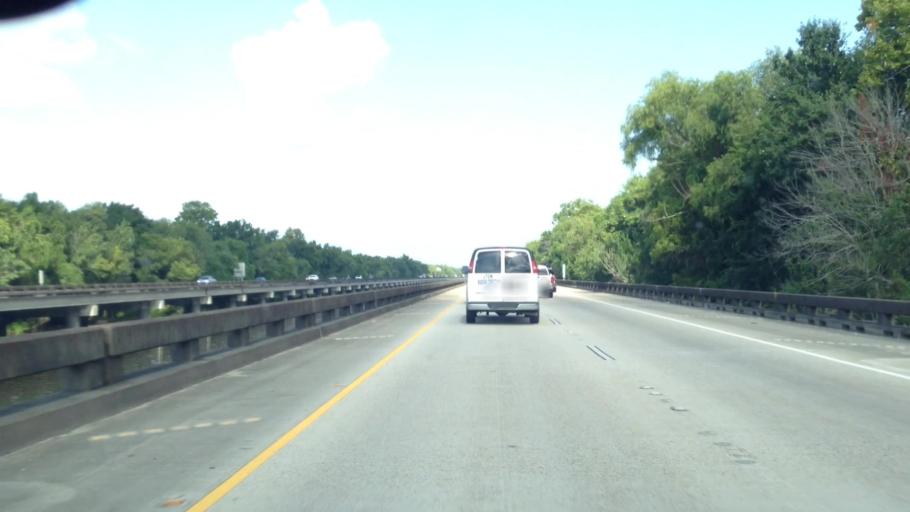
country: US
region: Louisiana
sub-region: Saint John the Baptist Parish
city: Montegut
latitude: 30.1085
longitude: -90.5140
